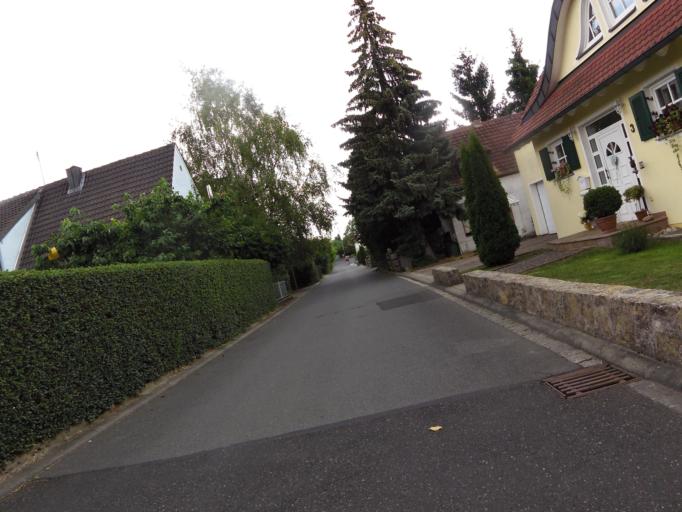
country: DE
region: Bavaria
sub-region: Regierungsbezirk Unterfranken
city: Eibelstadt
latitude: 49.7210
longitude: 9.9690
